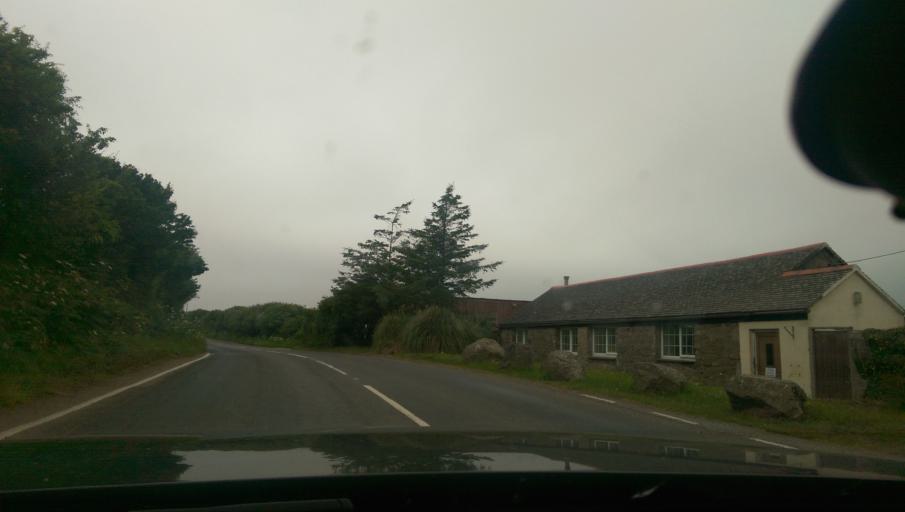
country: GB
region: England
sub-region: Cornwall
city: St. Buryan
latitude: 50.0911
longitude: -5.6274
